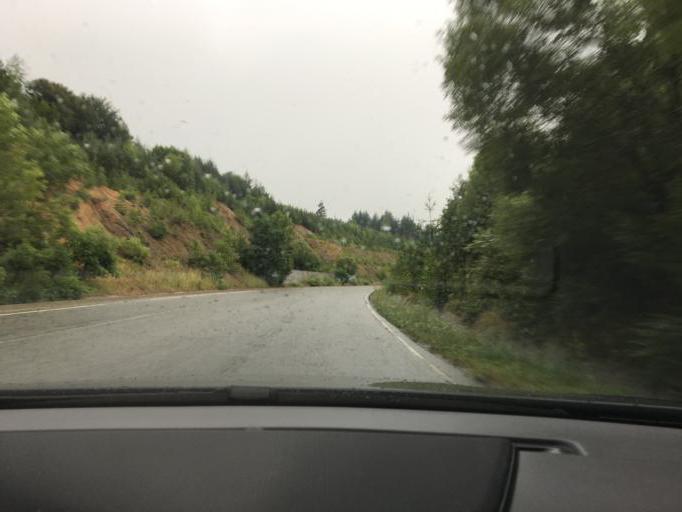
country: BG
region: Kyustendil
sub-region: Obshtina Kyustendil
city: Kyustendil
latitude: 42.2613
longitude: 22.5751
